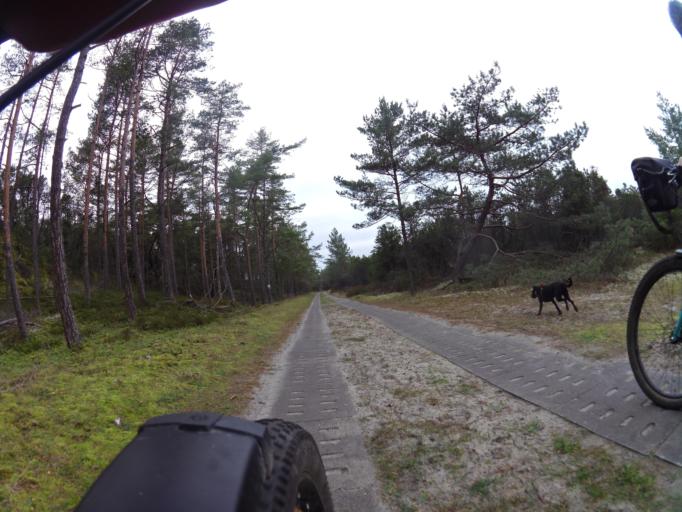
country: PL
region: Pomeranian Voivodeship
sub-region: Powiat pucki
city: Hel
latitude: 54.6273
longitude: 18.8141
